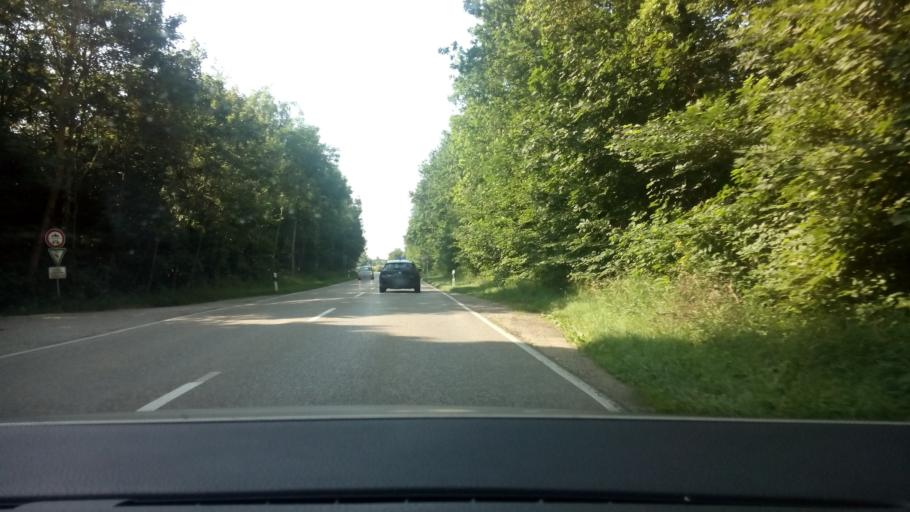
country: DE
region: Bavaria
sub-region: Upper Bavaria
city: Oberschleissheim
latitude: 48.2350
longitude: 11.5838
